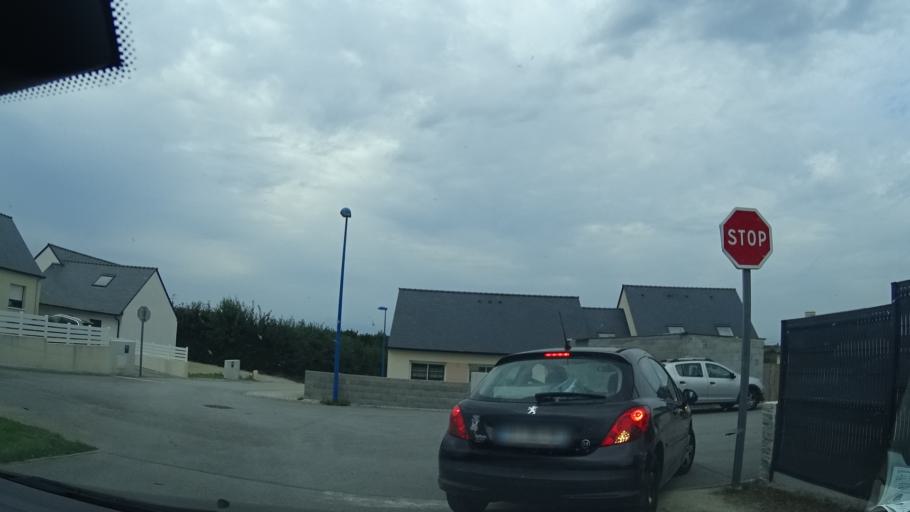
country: FR
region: Brittany
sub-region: Departement du Finistere
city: Plouarzel
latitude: 48.4356
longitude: -4.7323
